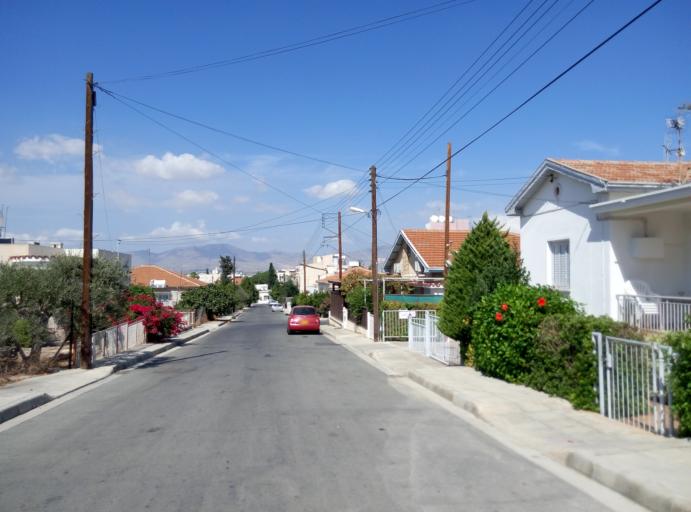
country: CY
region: Lefkosia
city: Nicosia
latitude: 35.1730
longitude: 33.3339
